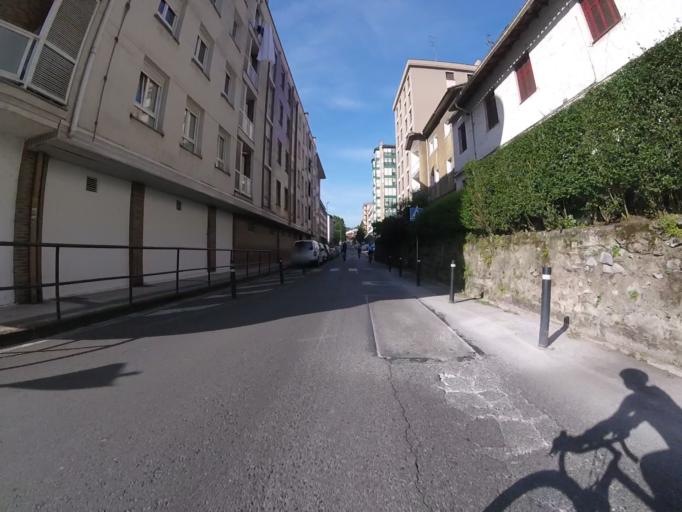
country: ES
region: Basque Country
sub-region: Provincia de Guipuzcoa
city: Villafranca de Ordizia
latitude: 43.0575
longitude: -2.1738
